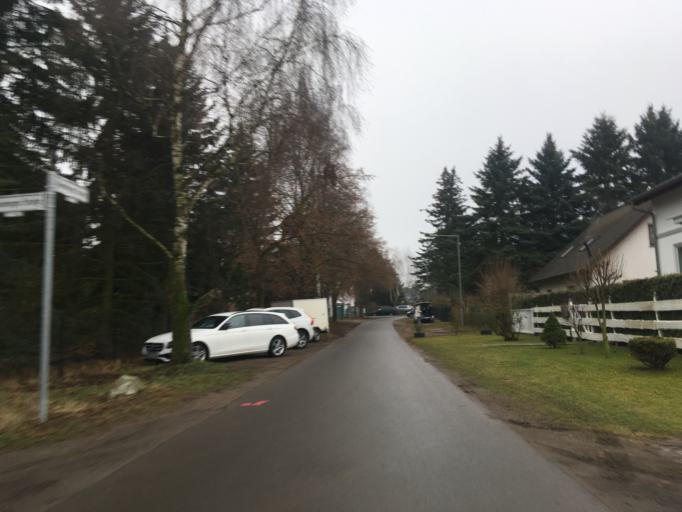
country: DE
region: Berlin
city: Buch
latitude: 52.6367
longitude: 13.5191
